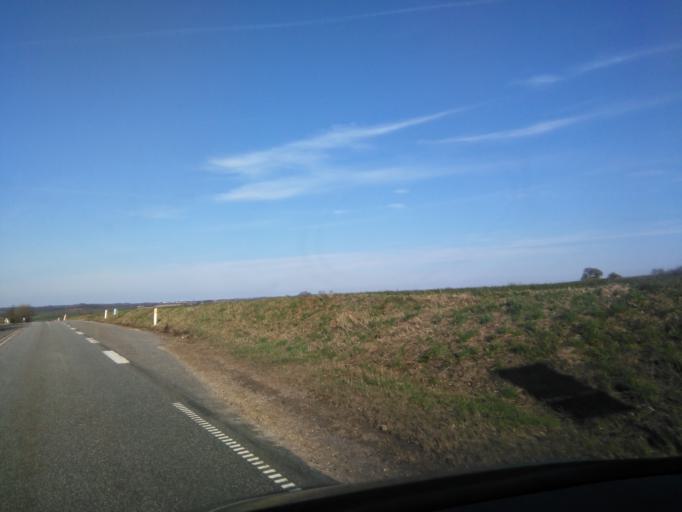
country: DK
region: Central Jutland
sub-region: Skanderborg Kommune
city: Ry
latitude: 56.0192
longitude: 9.8138
